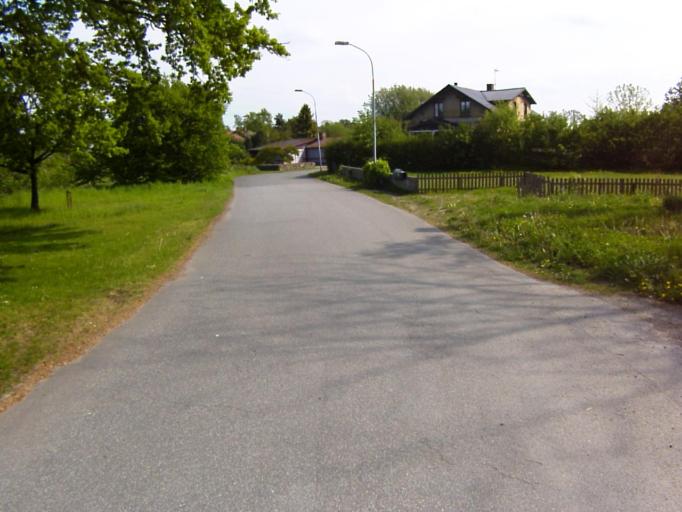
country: SE
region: Skane
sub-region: Kristianstads Kommun
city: Kristianstad
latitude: 56.0527
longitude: 14.0882
